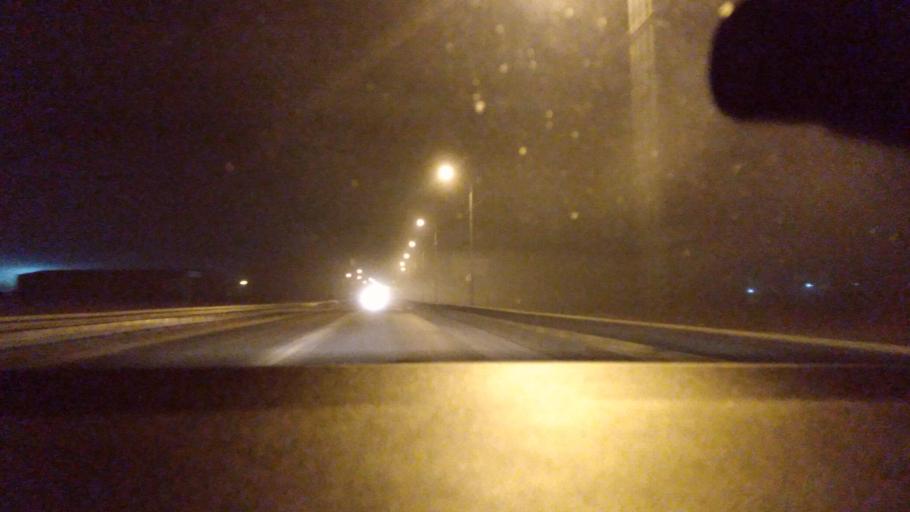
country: RU
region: Moskovskaya
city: Yegor'yevsk
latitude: 55.3913
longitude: 39.0752
